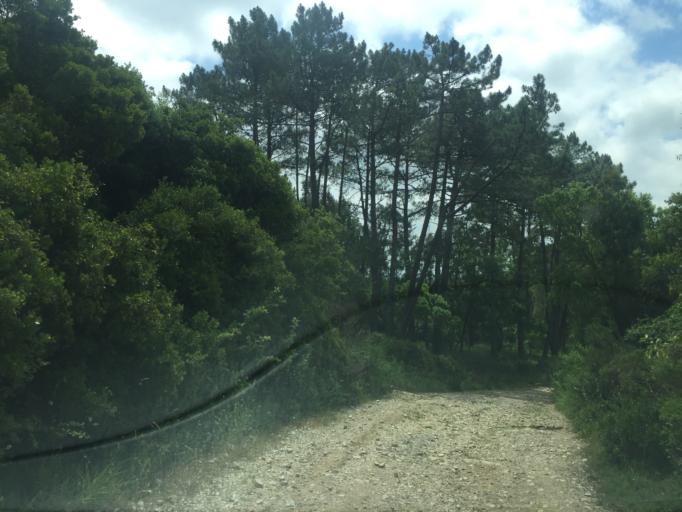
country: PT
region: Coimbra
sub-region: Figueira da Foz
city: Tavarede
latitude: 40.1856
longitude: -8.8226
